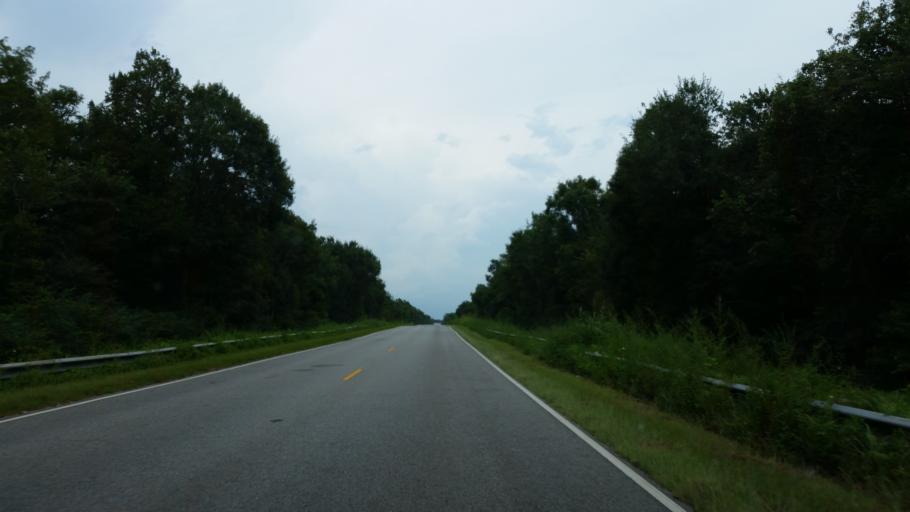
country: US
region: Florida
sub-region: Escambia County
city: Molino
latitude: 30.6678
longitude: -87.2765
